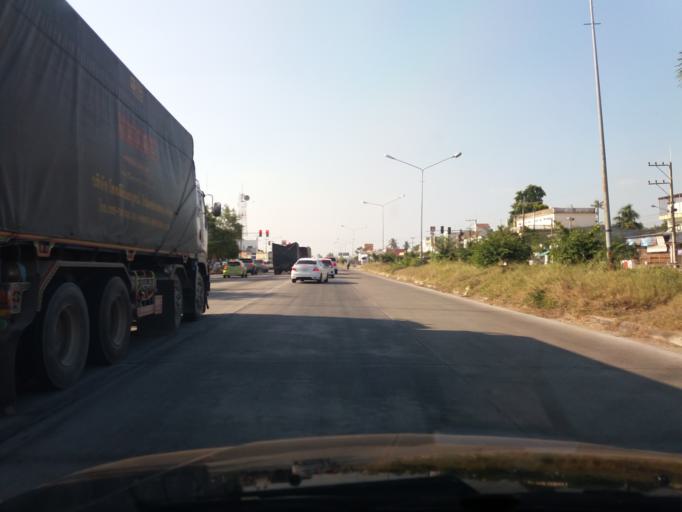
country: TH
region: Nakhon Sawan
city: Kao Liao
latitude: 15.7653
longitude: 99.9901
